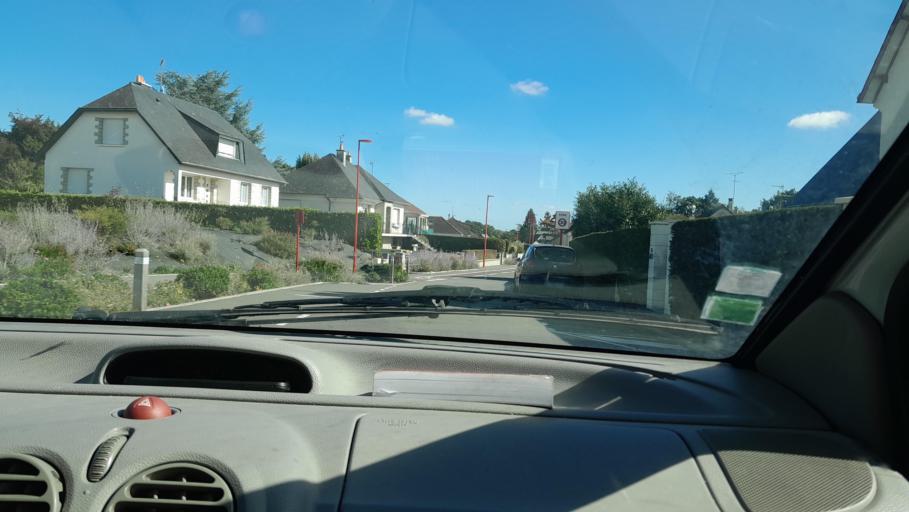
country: FR
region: Pays de la Loire
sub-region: Departement de la Mayenne
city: Cosse-le-Vivien
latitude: 47.9484
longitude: -0.9147
